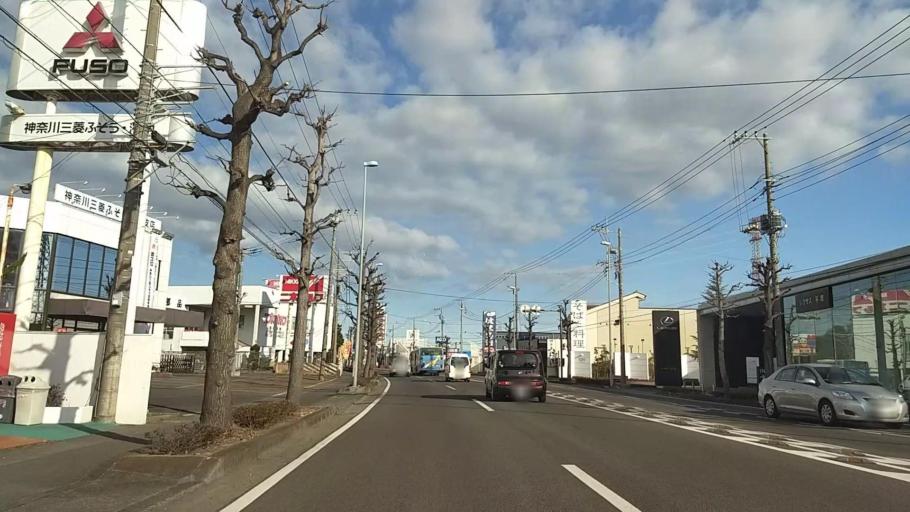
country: JP
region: Kanagawa
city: Hiratsuka
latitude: 35.3638
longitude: 139.3613
